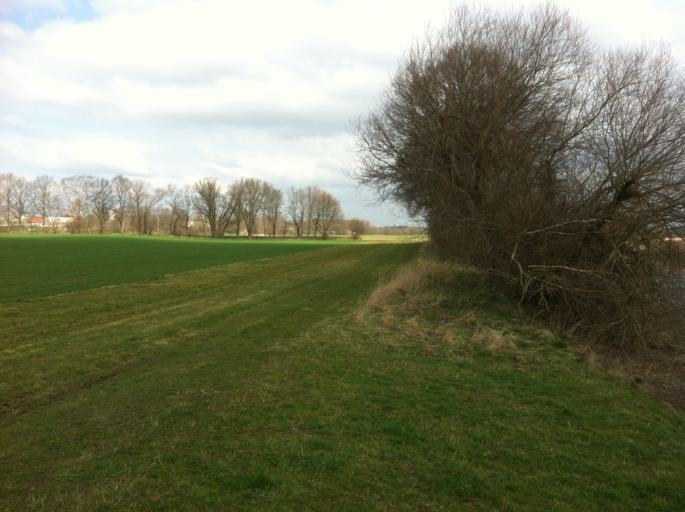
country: DE
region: Saxony
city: Trebsen
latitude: 51.3174
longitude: 12.7456
